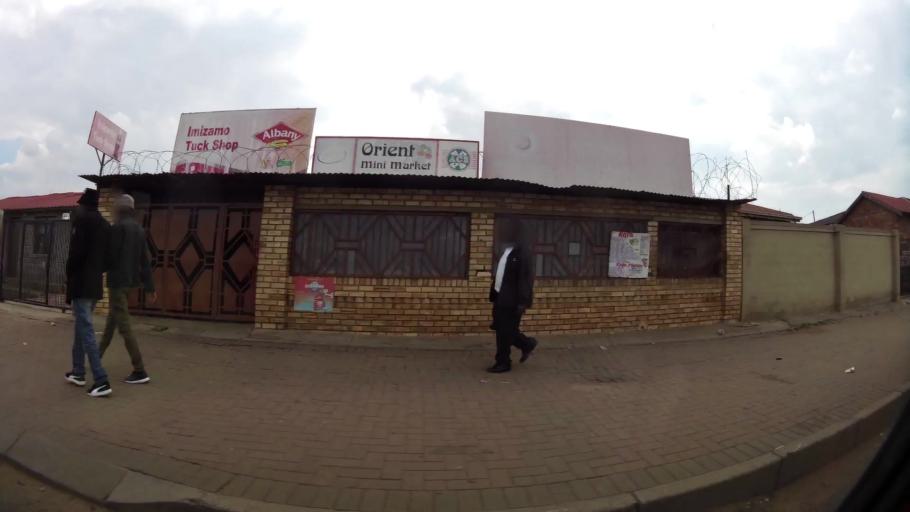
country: ZA
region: Gauteng
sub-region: City of Johannesburg Metropolitan Municipality
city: Soweto
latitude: -26.2374
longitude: 27.8601
